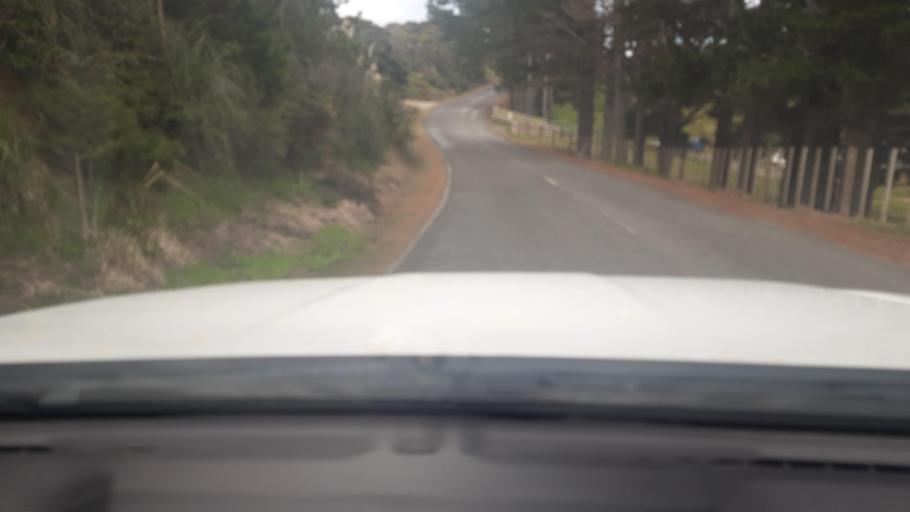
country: NZ
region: Northland
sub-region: Far North District
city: Ahipara
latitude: -35.2731
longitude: 173.2102
